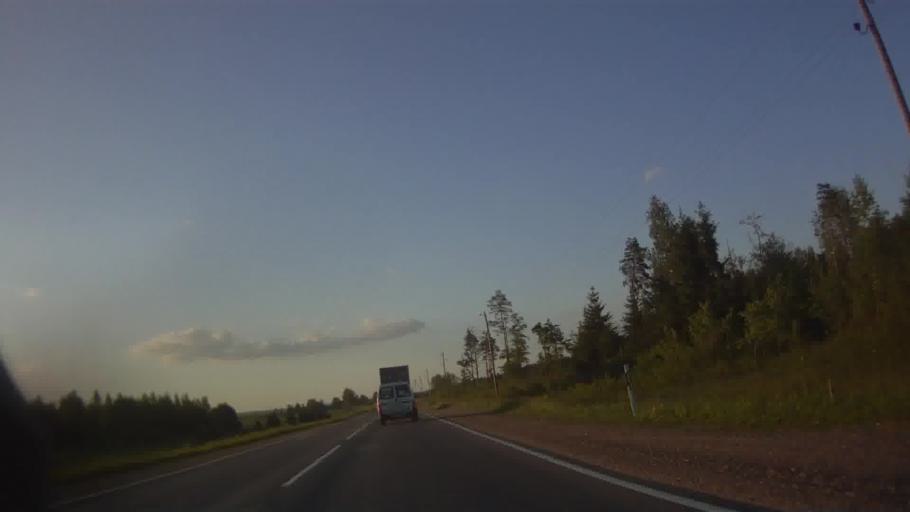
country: LV
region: Salas
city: Sala
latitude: 56.5699
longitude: 25.7758
